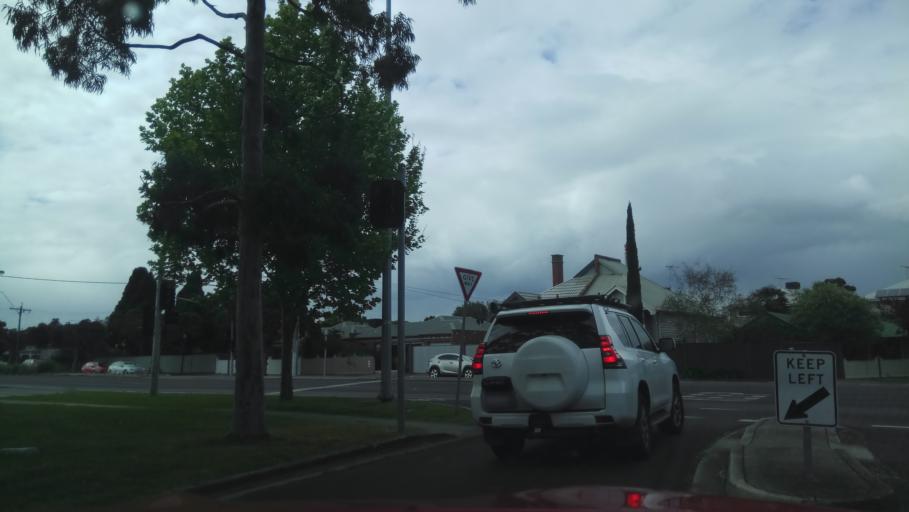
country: AU
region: Victoria
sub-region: Hobsons Bay
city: Newport
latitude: -37.8494
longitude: 144.8875
